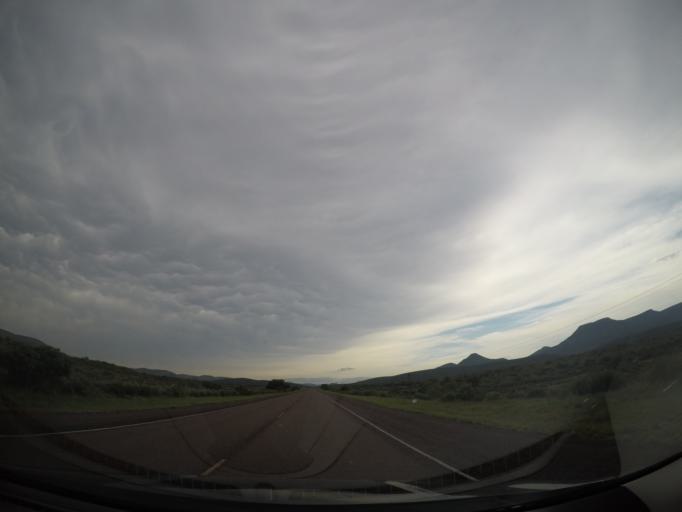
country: US
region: Texas
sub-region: Terrell County
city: Sanderson
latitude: 30.2044
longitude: -102.9667
